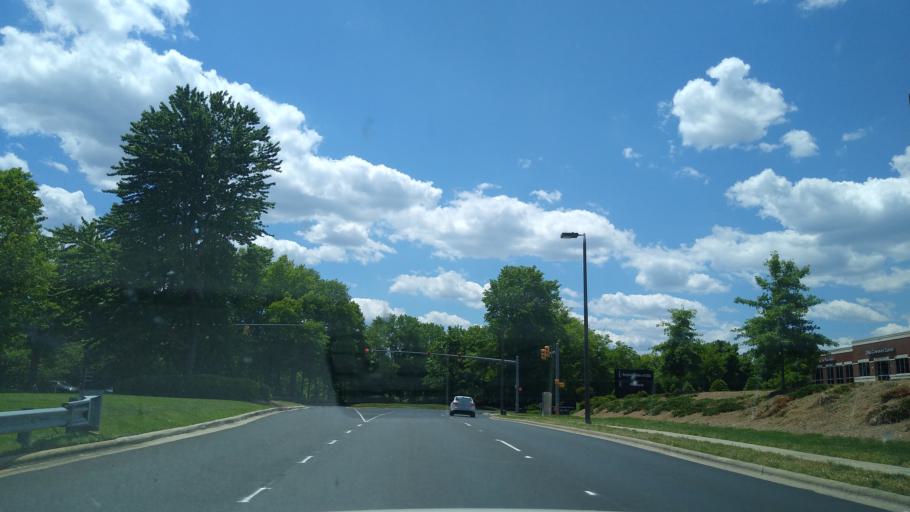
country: US
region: North Carolina
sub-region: Guilford County
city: Greensboro
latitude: 36.0908
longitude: -79.8222
